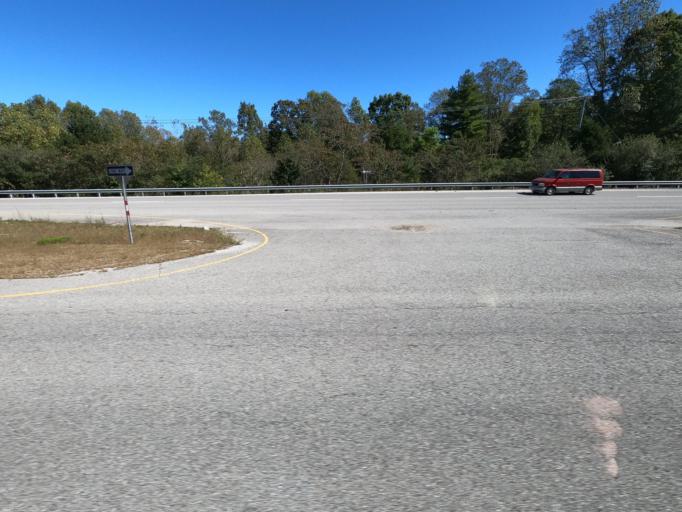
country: US
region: Tennessee
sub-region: Maury County
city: Mount Pleasant
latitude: 35.4536
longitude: -87.2671
